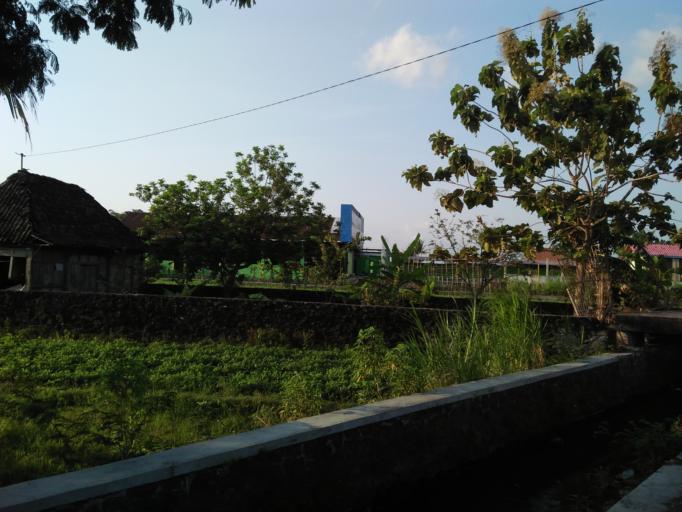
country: ID
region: Daerah Istimewa Yogyakarta
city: Pundong
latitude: -7.9352
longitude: 110.3418
